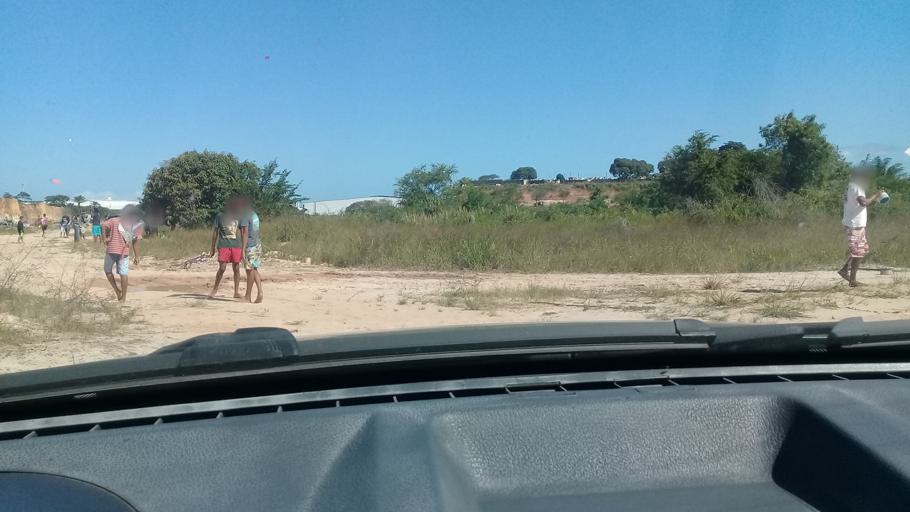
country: BR
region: Pernambuco
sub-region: Jaboatao Dos Guararapes
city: Jaboatao
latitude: -8.1475
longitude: -34.9498
